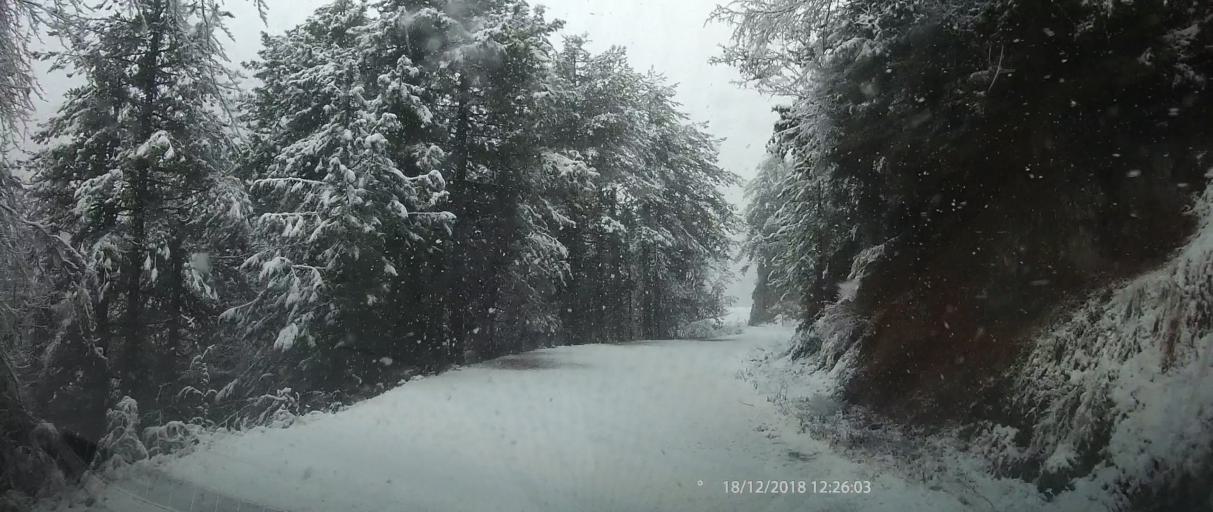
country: GR
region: Central Macedonia
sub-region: Nomos Pierias
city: Litochoro
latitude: 40.0888
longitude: 22.4123
